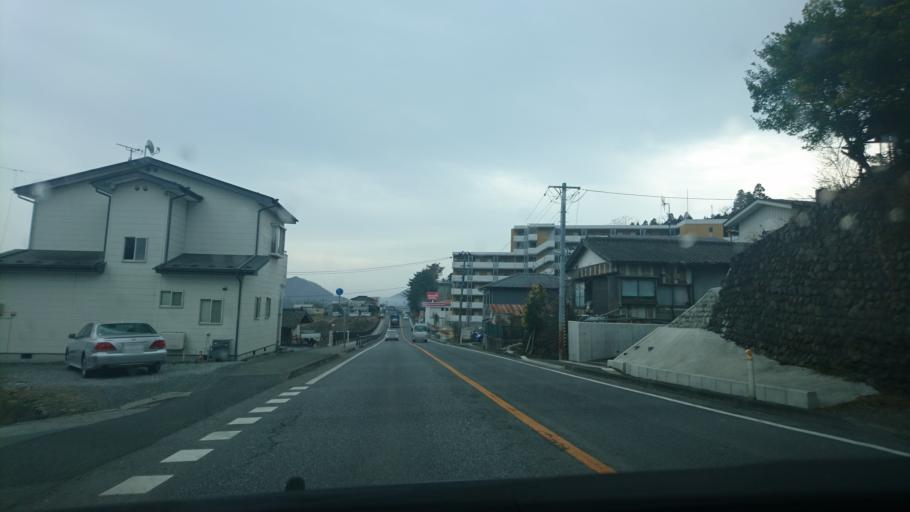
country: JP
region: Iwate
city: Ofunato
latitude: 39.0473
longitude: 141.7211
